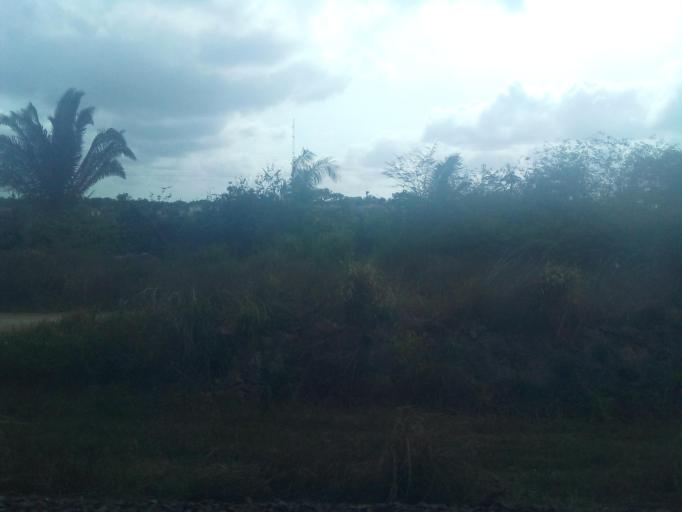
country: BR
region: Maranhao
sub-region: Sao Luis
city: Sao Luis
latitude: -2.6414
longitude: -44.3055
